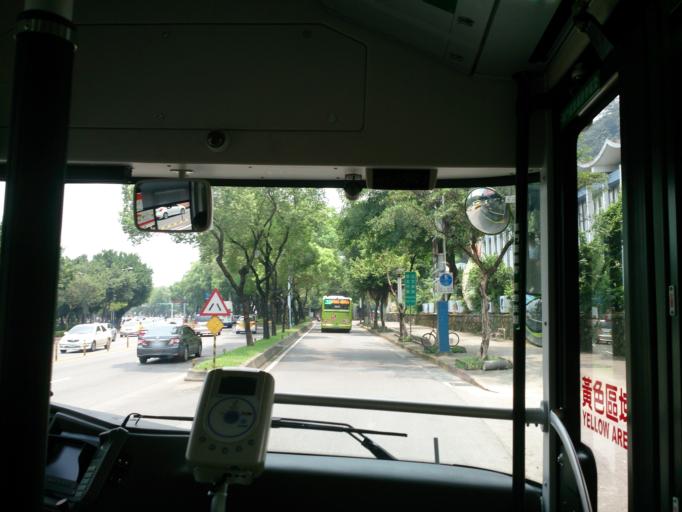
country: TW
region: Taipei
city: Taipei
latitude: 25.0819
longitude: 121.5253
